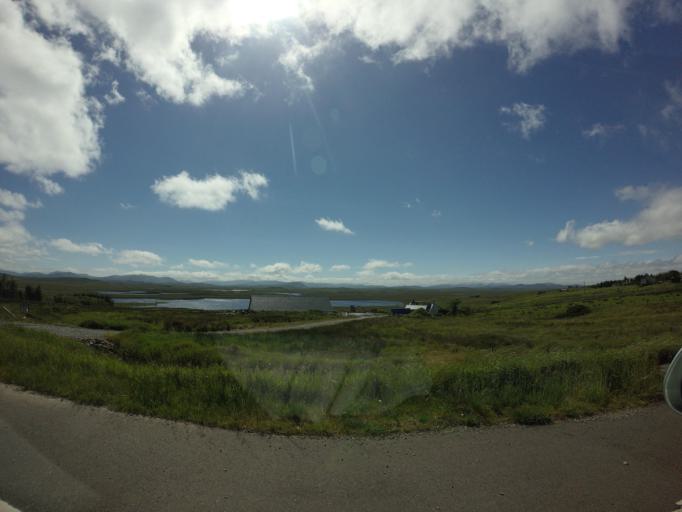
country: GB
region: Scotland
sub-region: Eilean Siar
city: Stornoway
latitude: 58.1703
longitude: -6.5687
